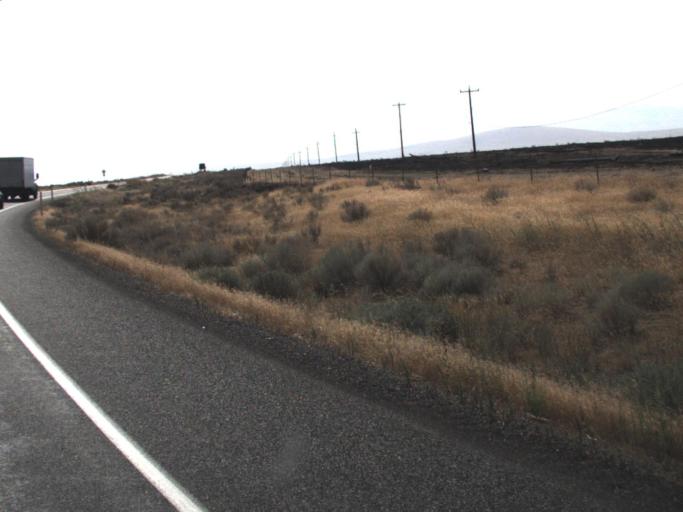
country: US
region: Washington
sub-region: Grant County
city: Desert Aire
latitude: 46.6019
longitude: -119.7274
